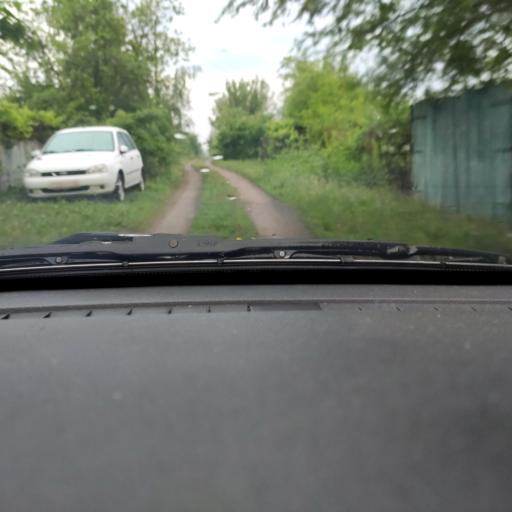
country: RU
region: Voronezj
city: Maslovka
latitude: 51.4907
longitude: 39.2178
